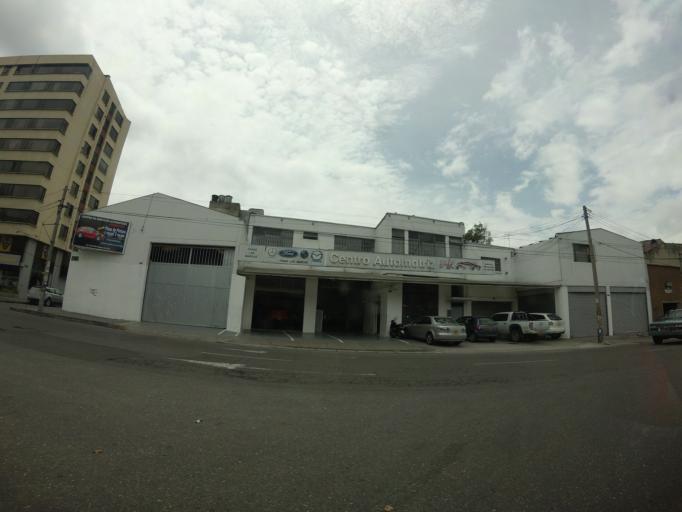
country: CO
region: Bogota D.C.
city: Bogota
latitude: 4.6214
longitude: -74.0753
